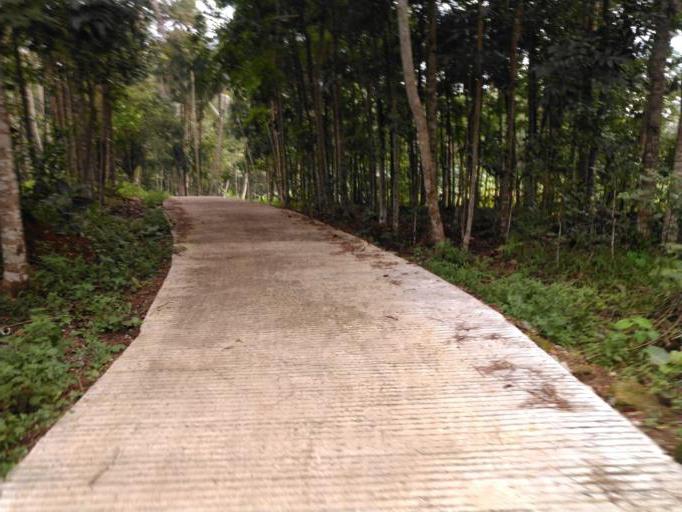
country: ID
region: West Java
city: Cigugur
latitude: -7.6449
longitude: 108.4217
